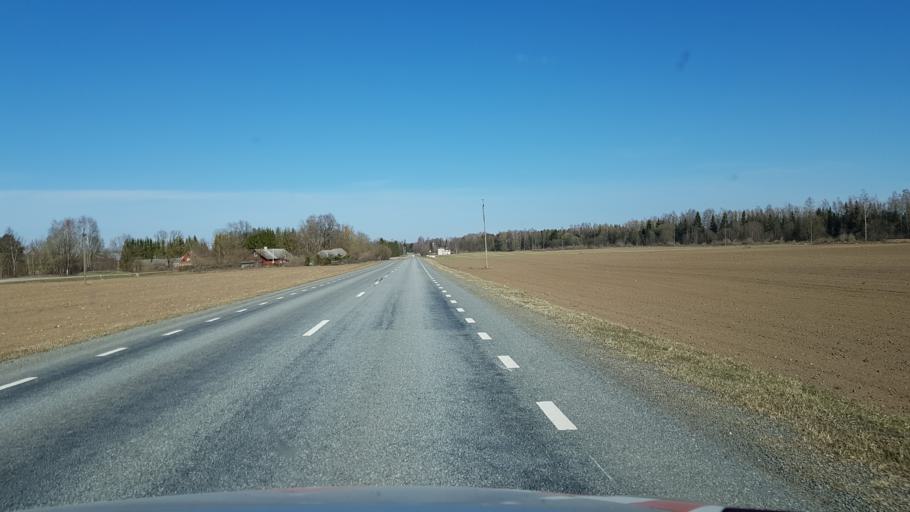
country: EE
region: Jaervamaa
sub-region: Jaerva-Jaani vald
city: Jarva-Jaani
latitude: 59.1031
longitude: 25.9926
